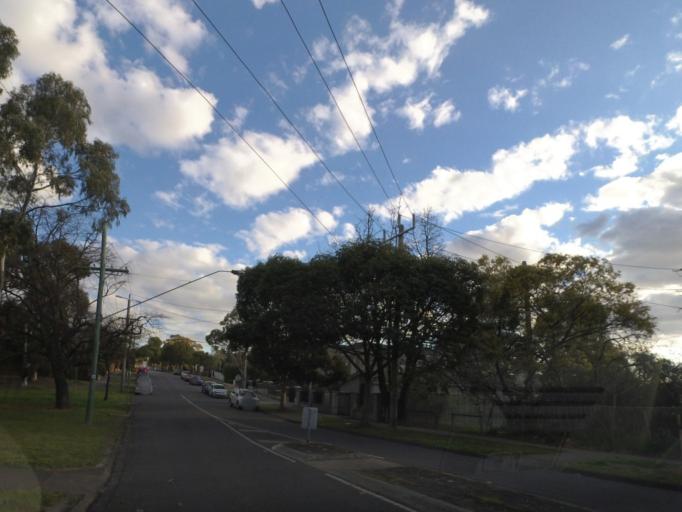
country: AU
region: Victoria
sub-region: Boroondara
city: Canterbury
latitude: -37.8424
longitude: 145.0896
